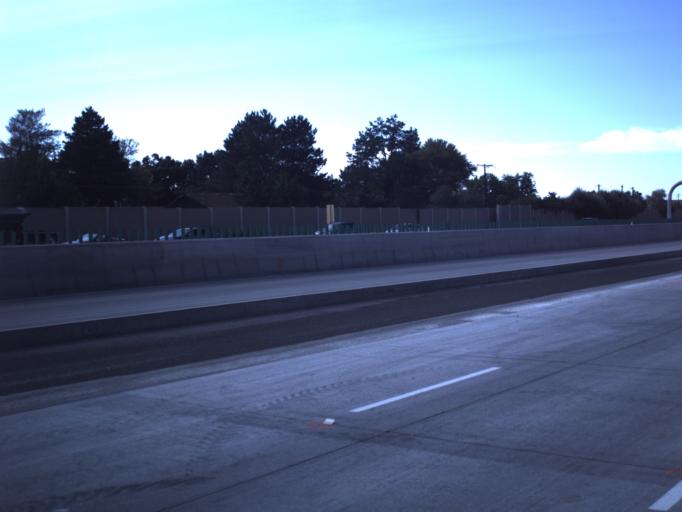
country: US
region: Utah
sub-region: Salt Lake County
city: Taylorsville
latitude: 40.6841
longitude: -111.9512
